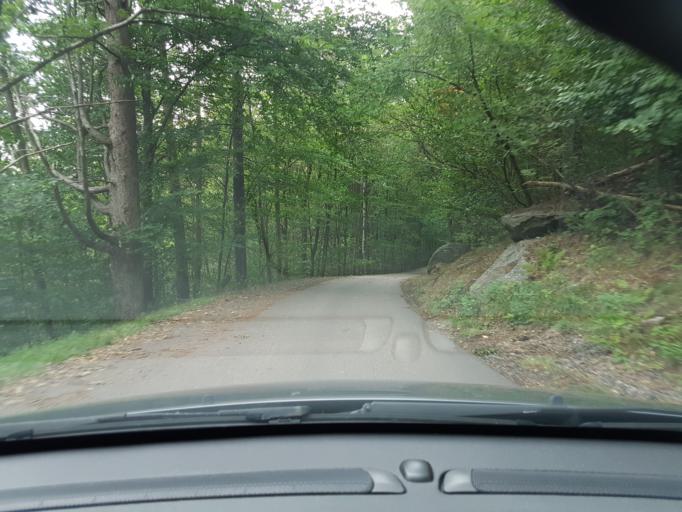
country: SE
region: Vaestra Goetaland
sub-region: Ale Kommun
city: Surte
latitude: 57.8298
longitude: 12.0242
